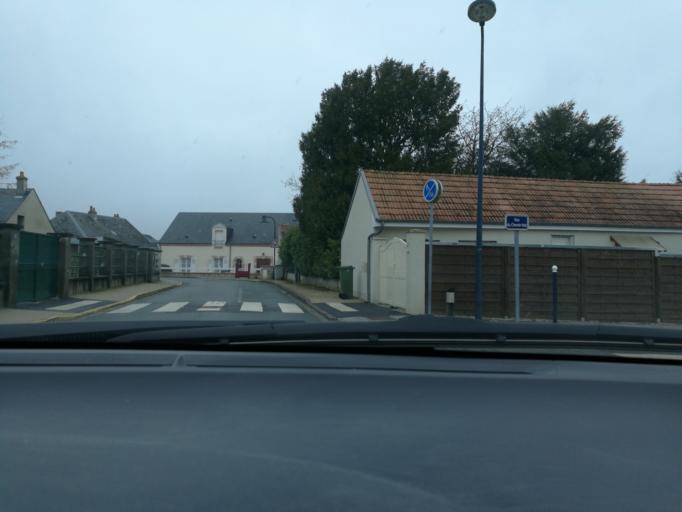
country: FR
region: Centre
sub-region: Departement du Loiret
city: Semoy
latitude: 47.9327
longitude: 1.9501
